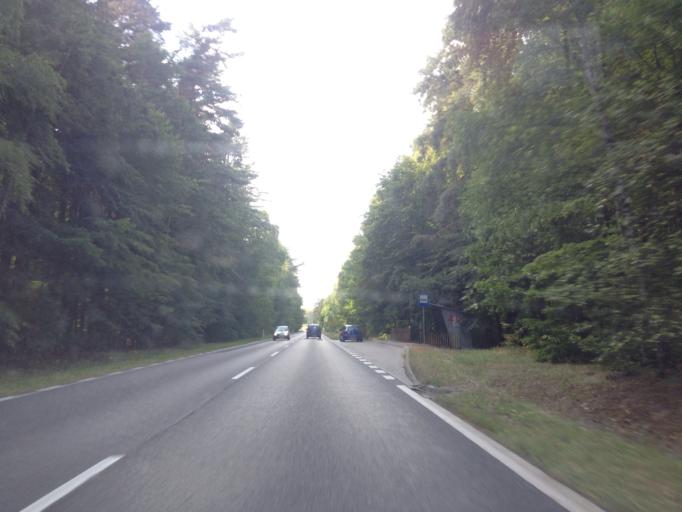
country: PL
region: Kujawsko-Pomorskie
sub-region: Powiat swiecki
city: Swiekatowo
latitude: 53.4832
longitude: 18.1319
